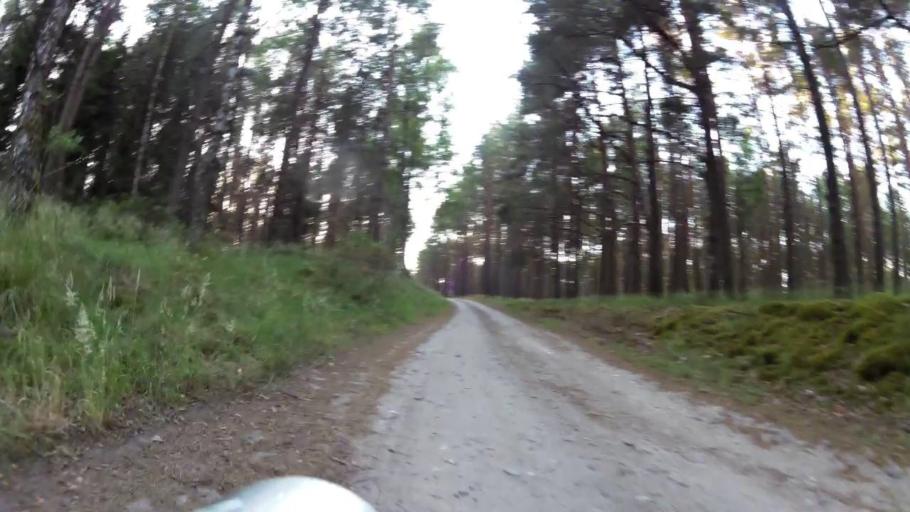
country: PL
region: West Pomeranian Voivodeship
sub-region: Powiat szczecinecki
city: Szczecinek
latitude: 53.8190
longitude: 16.6943
